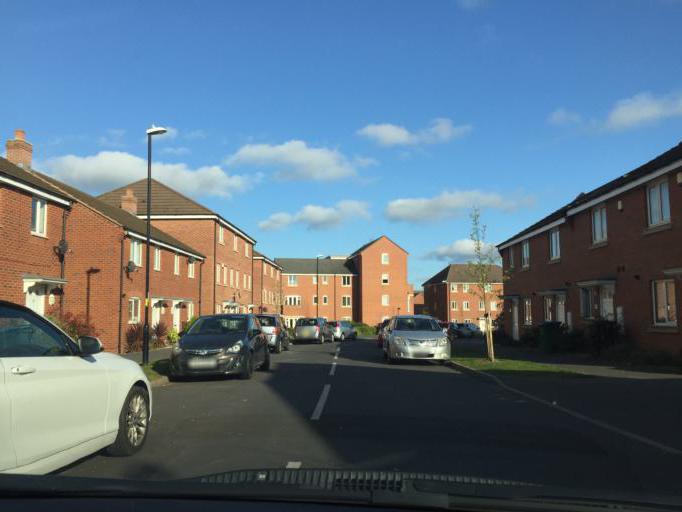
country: GB
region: England
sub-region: Coventry
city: Coventry
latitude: 52.4024
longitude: -1.4850
